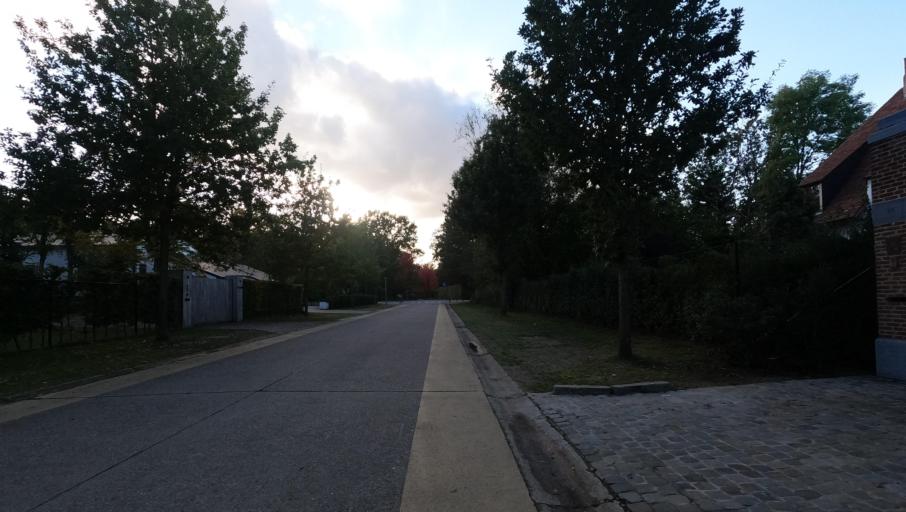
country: BE
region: Flanders
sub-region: Provincie Antwerpen
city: Schilde
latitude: 51.2366
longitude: 4.5582
